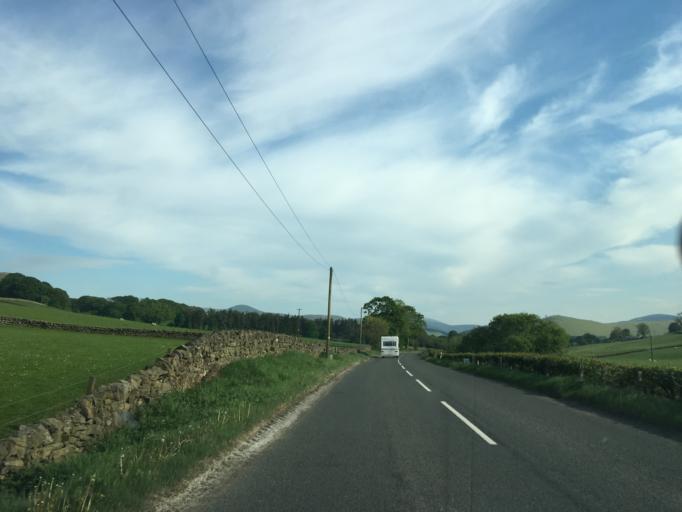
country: GB
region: Scotland
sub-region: South Lanarkshire
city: Biggar
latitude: 55.6261
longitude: -3.4161
